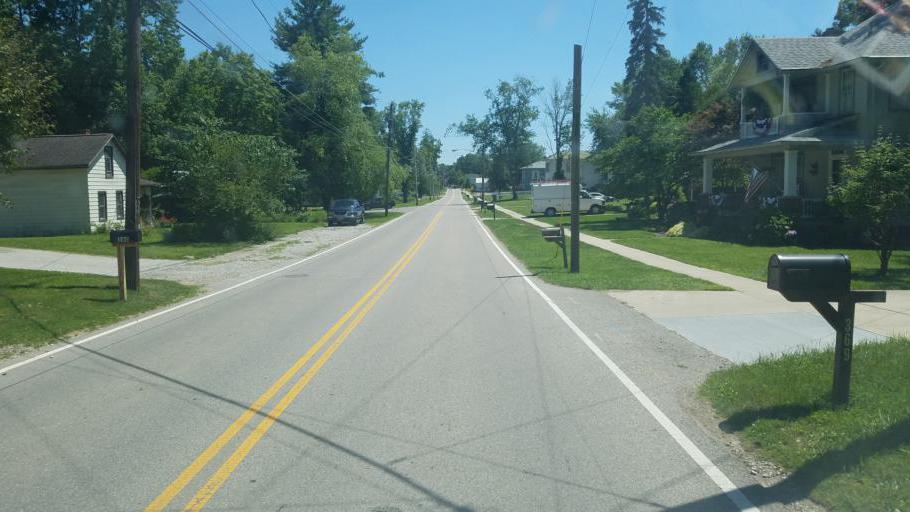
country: US
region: Ohio
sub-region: Delaware County
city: Sunbury
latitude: 40.2226
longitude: -82.8820
